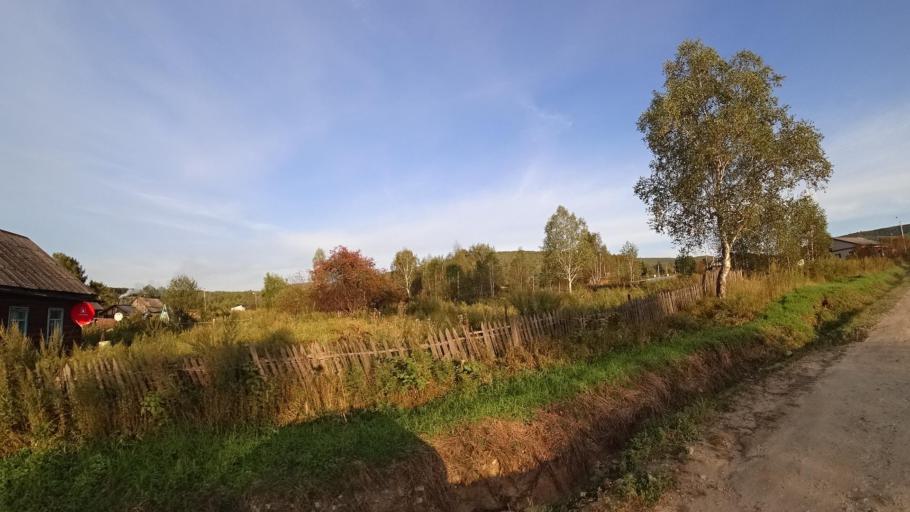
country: RU
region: Jewish Autonomous Oblast
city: Kul'dur
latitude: 49.2049
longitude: 131.6400
